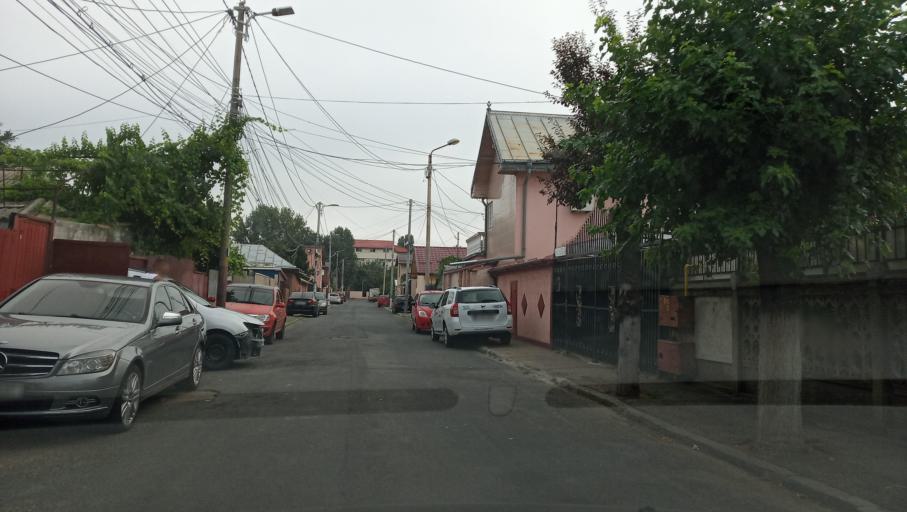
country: RO
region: Ilfov
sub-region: Comuna Pantelimon
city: Pantelimon
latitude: 44.4252
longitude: 26.2004
